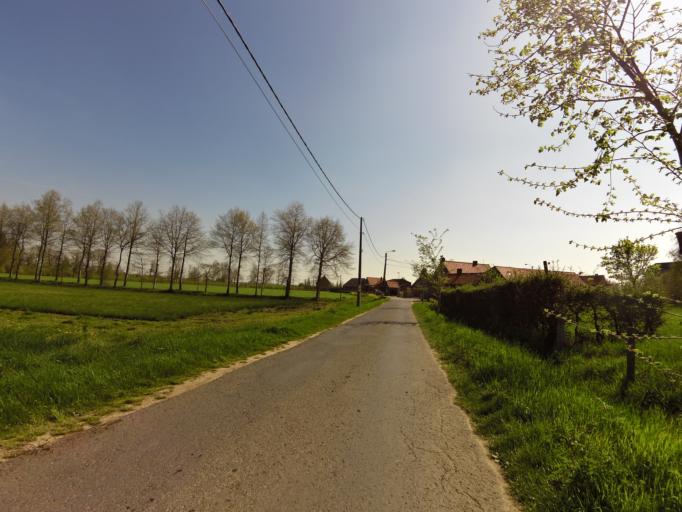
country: BE
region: Flanders
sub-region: Provincie West-Vlaanderen
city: Kortemark
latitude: 51.0567
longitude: 3.0203
